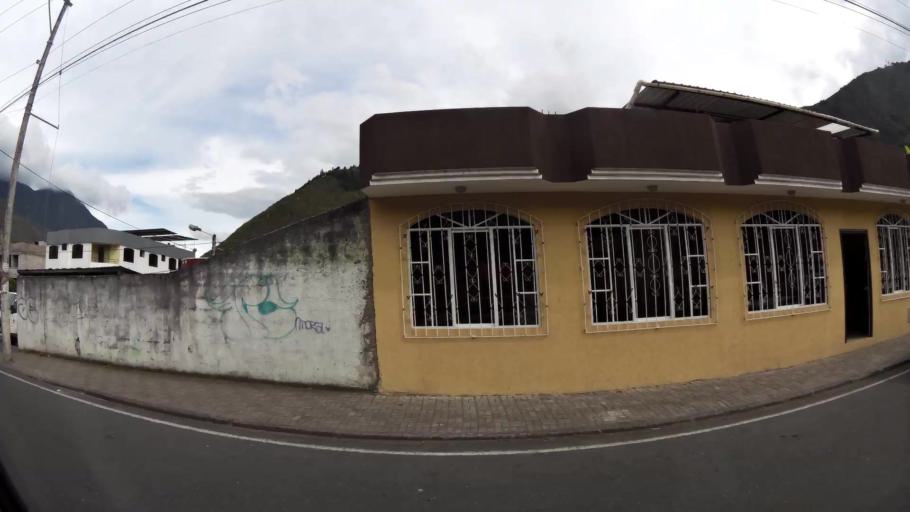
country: EC
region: Tungurahua
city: Banos
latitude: -1.3946
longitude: -78.4218
